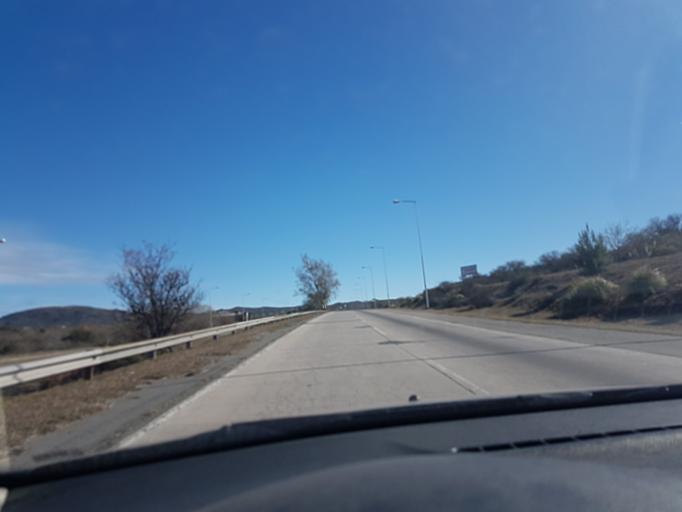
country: AR
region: Cordoba
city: Villa Carlos Paz
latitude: -31.4402
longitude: -64.4404
